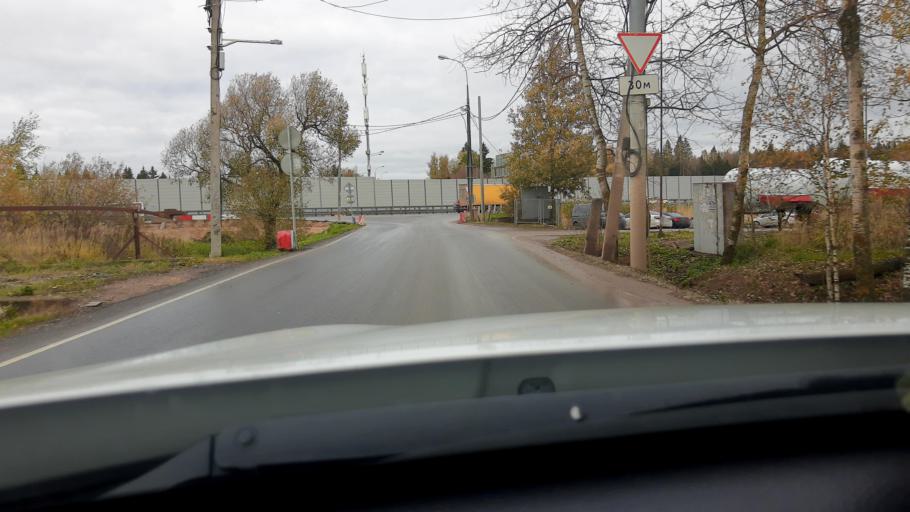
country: RU
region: Moskovskaya
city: Annino
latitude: 55.5782
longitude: 37.2366
